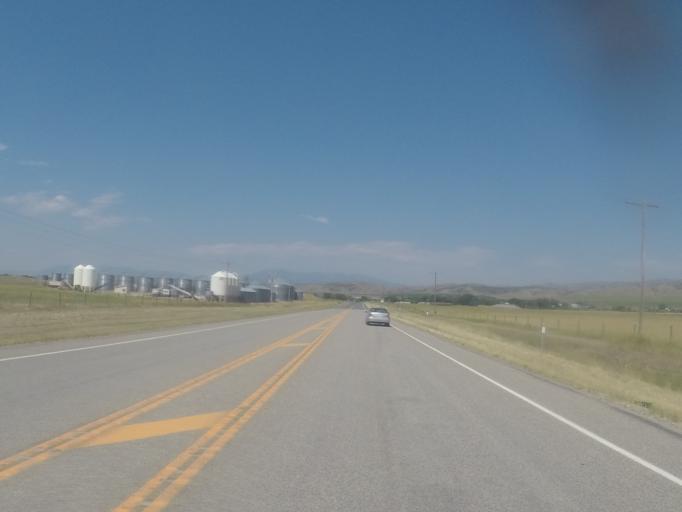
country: US
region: Montana
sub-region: Broadwater County
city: Townsend
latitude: 46.1635
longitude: -111.4548
